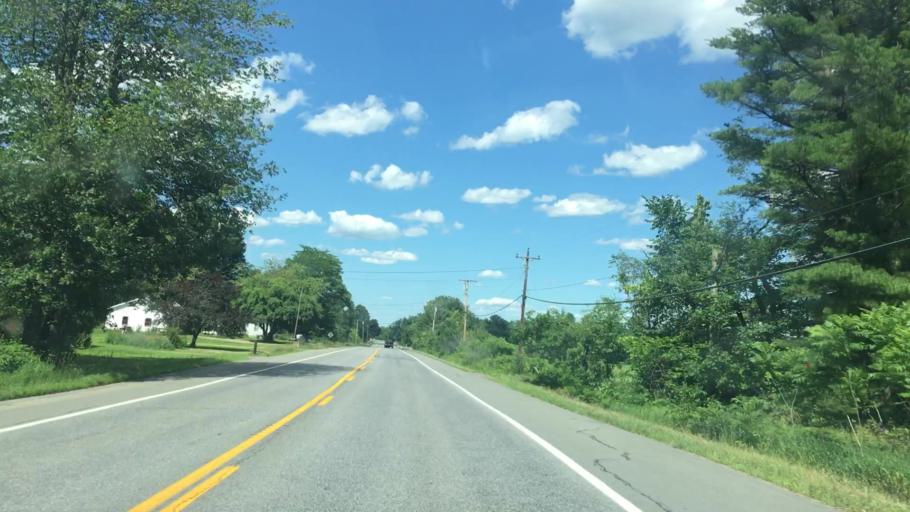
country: US
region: Maine
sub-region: Franklin County
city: New Sharon
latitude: 44.6230
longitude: -70.0574
